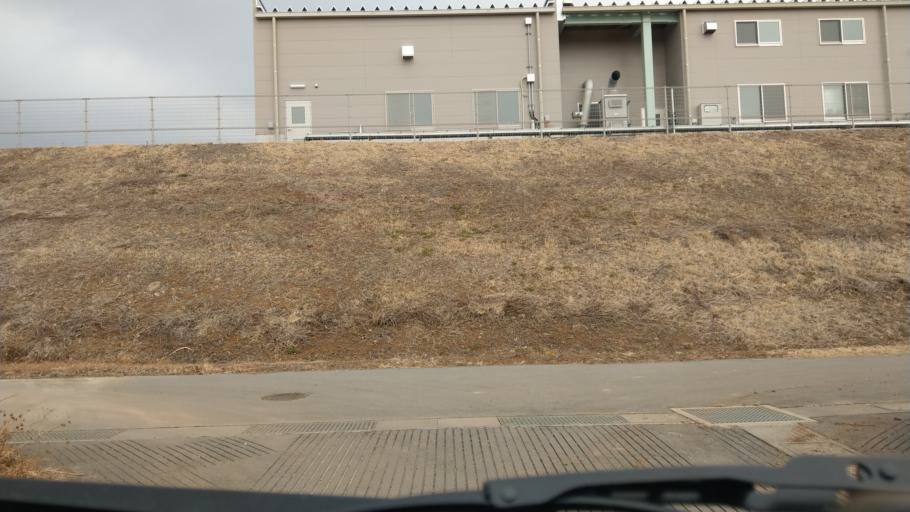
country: JP
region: Nagano
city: Komoro
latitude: 36.3453
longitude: 138.4006
